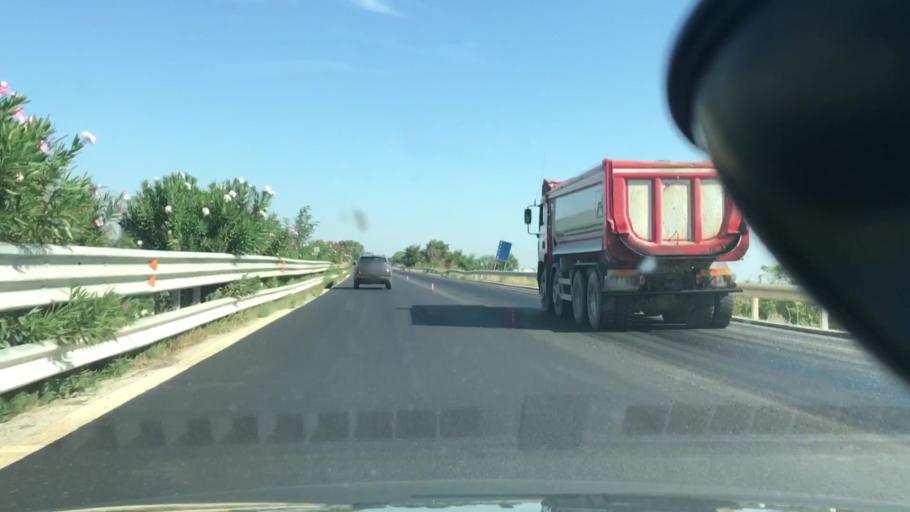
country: IT
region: Apulia
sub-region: Provincia di Foggia
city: Ascoli Satriano
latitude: 41.2694
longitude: 15.5520
